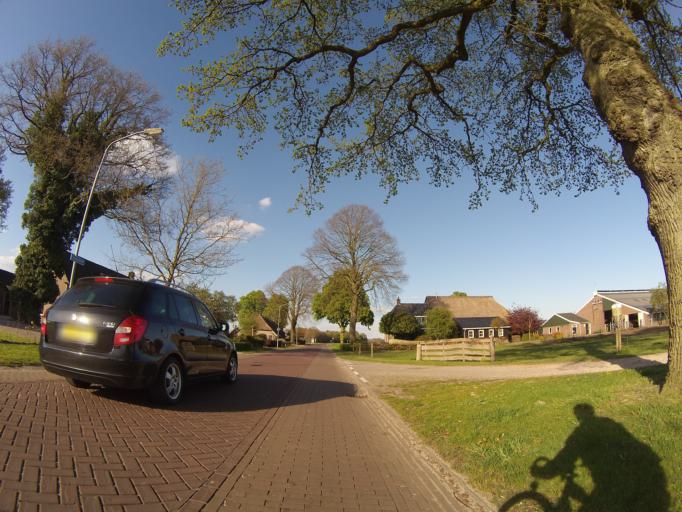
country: NL
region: Drenthe
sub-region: Gemeente Coevorden
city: Dalen
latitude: 52.7525
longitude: 6.6953
